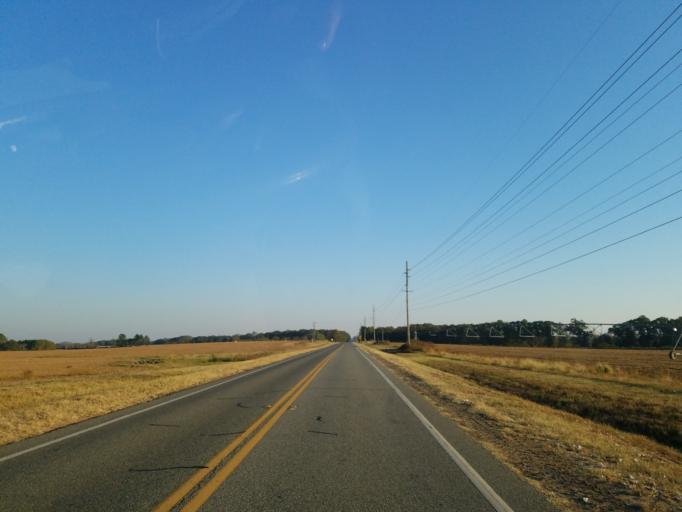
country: US
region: Georgia
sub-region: Crisp County
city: Cordele
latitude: 31.9115
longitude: -83.7066
